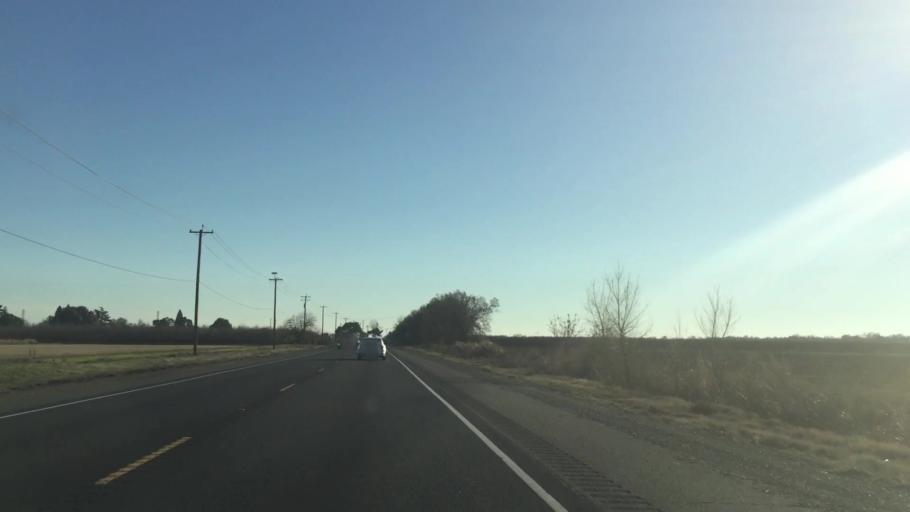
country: US
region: California
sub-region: Sutter County
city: Live Oak
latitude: 39.3270
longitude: -121.5969
